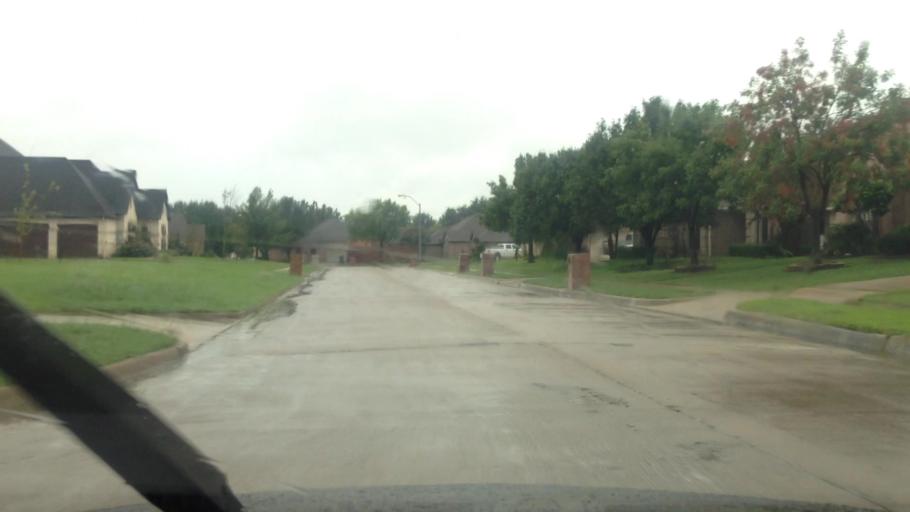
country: US
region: Texas
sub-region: Tarrant County
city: Colleyville
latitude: 32.9022
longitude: -97.2040
